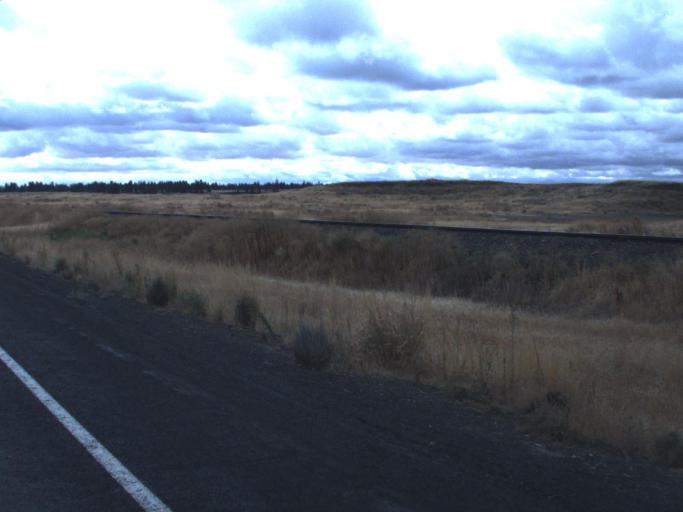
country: US
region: Washington
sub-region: Lincoln County
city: Davenport
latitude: 47.6928
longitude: -118.3928
